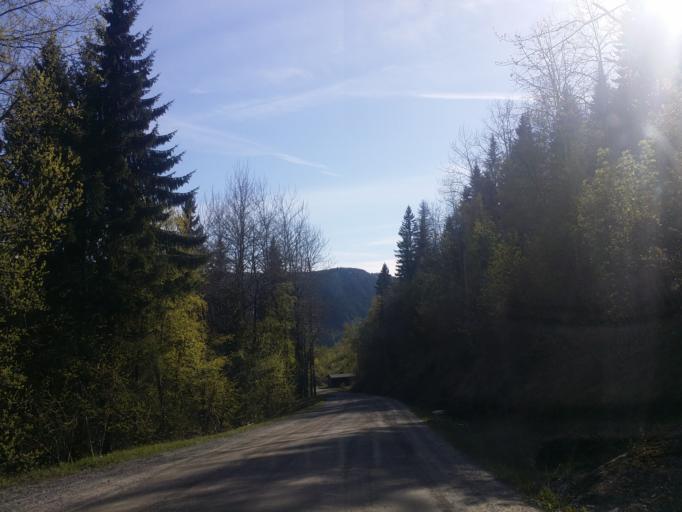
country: NO
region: Telemark
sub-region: Seljord
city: Seljord
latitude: 59.6116
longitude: 8.6893
